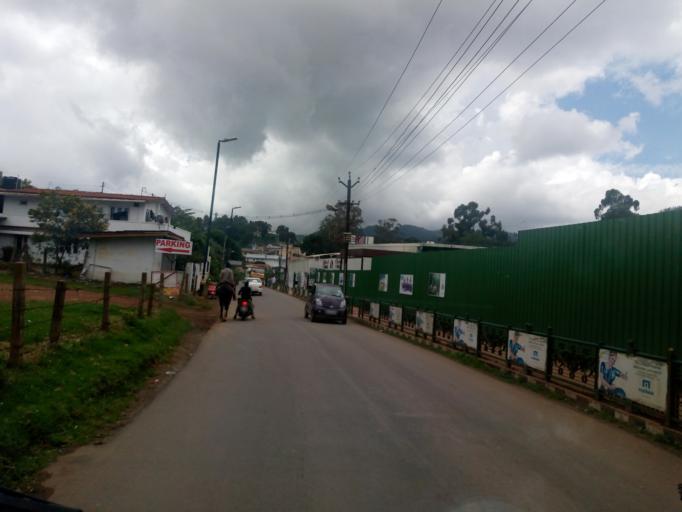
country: IN
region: Tamil Nadu
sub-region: Nilgiri
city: Ooty
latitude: 11.4040
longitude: 76.6933
